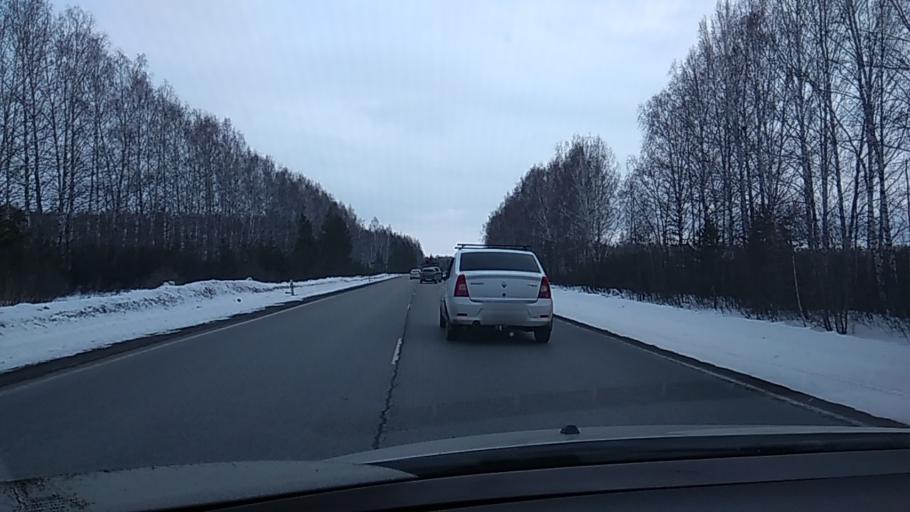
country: RU
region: Sverdlovsk
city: Sovkhoznyy
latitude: 56.5298
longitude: 61.4171
